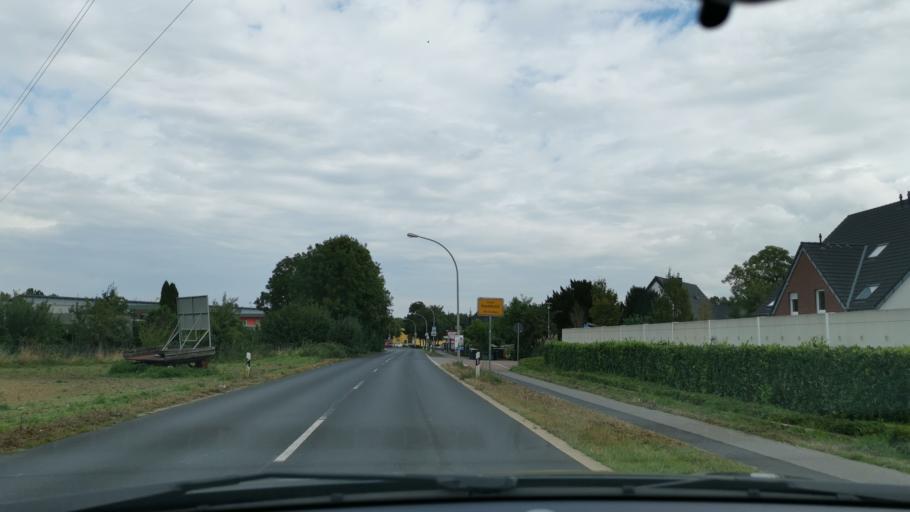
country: DE
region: North Rhine-Westphalia
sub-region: Regierungsbezirk Dusseldorf
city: Grevenbroich
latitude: 51.0845
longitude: 6.5736
